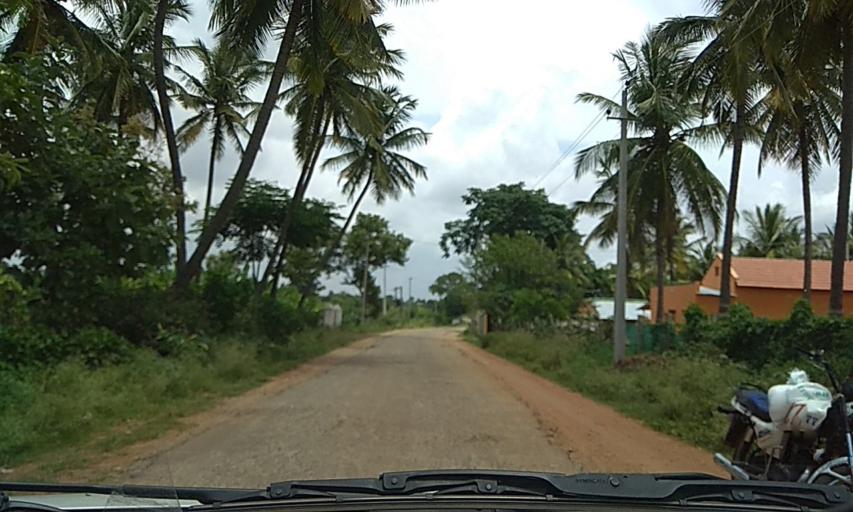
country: IN
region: Karnataka
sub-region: Chamrajnagar
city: Gundlupet
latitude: 11.8826
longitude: 76.6854
